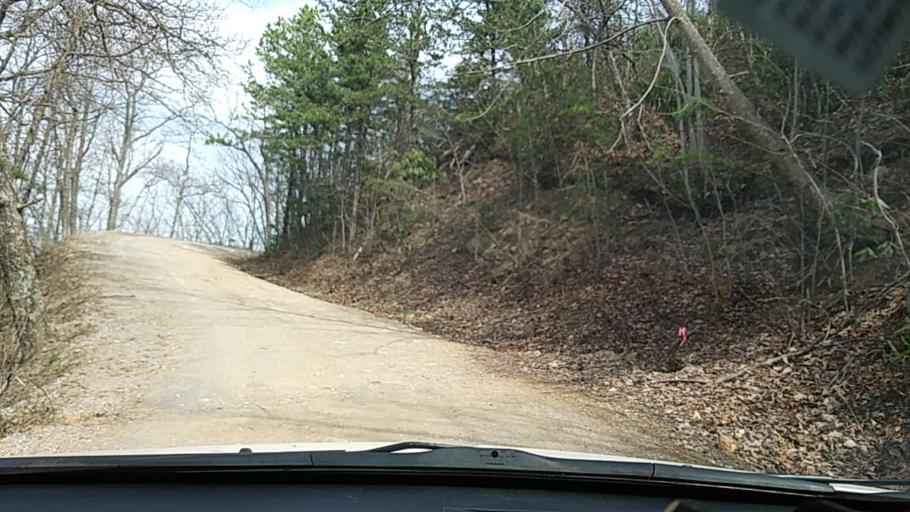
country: US
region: Tennessee
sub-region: Greene County
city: Tusculum
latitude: 36.0882
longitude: -82.6876
